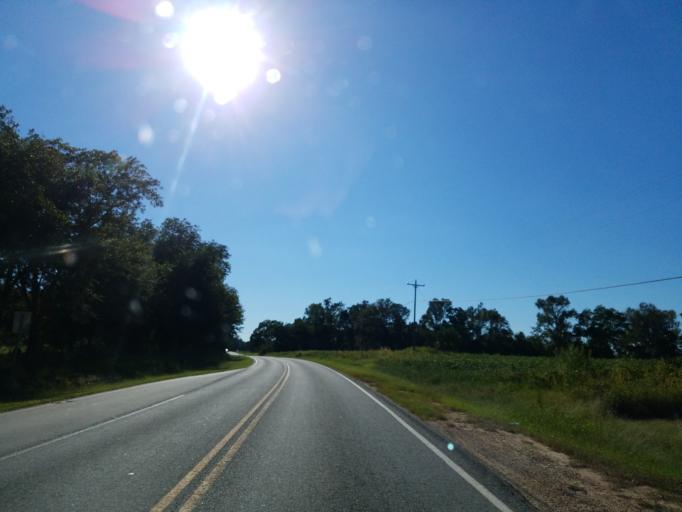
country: US
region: Georgia
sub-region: Dooly County
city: Unadilla
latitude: 32.2606
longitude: -83.7527
